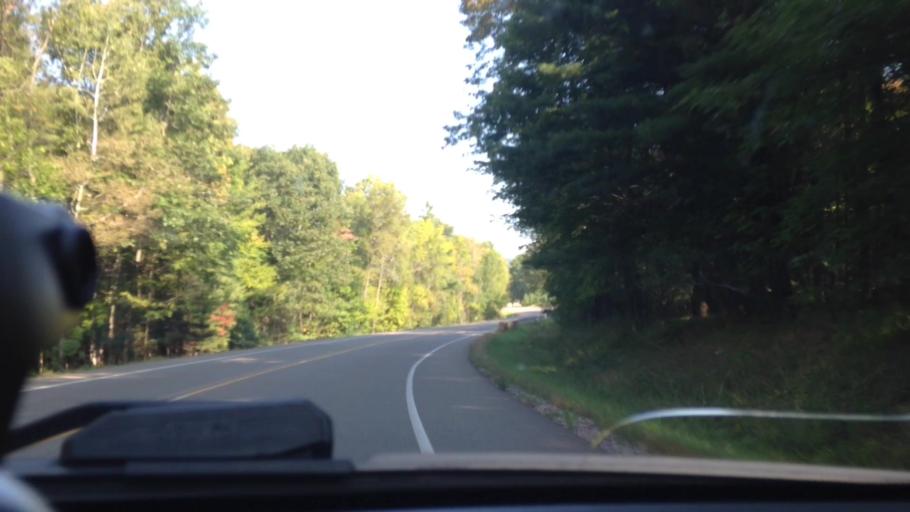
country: US
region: Michigan
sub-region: Dickinson County
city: Quinnesec
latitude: 45.8242
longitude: -87.9919
